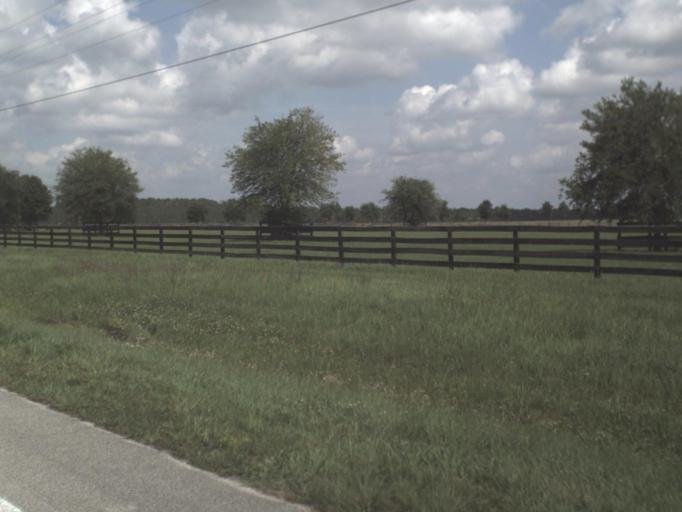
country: US
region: Florida
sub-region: Saint Johns County
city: Saint Augustine Shores
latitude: 29.7258
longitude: -81.4436
